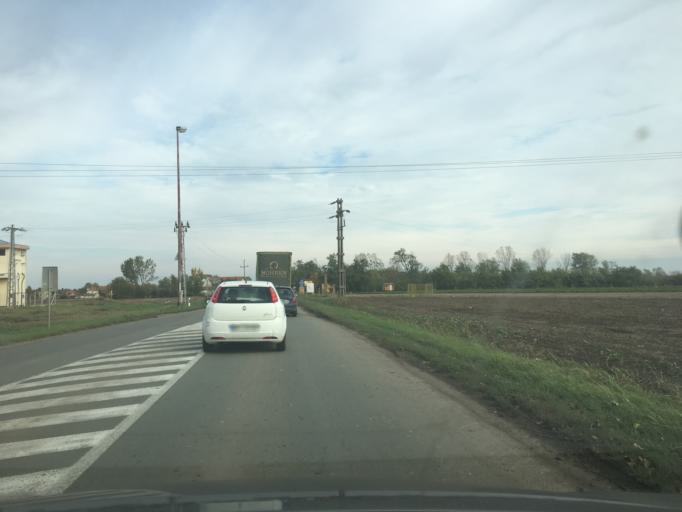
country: RS
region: Autonomna Pokrajina Vojvodina
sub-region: Juznobacki Okrug
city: Zabalj
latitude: 45.3560
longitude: 20.0646
